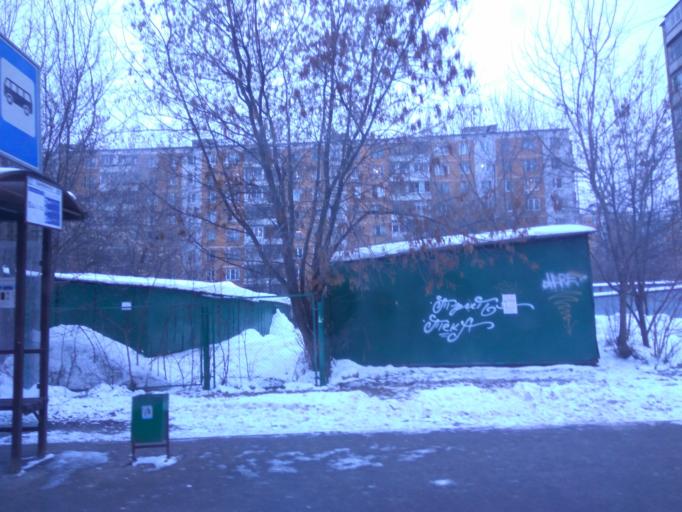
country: RU
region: Moscow
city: Gol'yanovo
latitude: 55.8145
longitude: 37.8280
